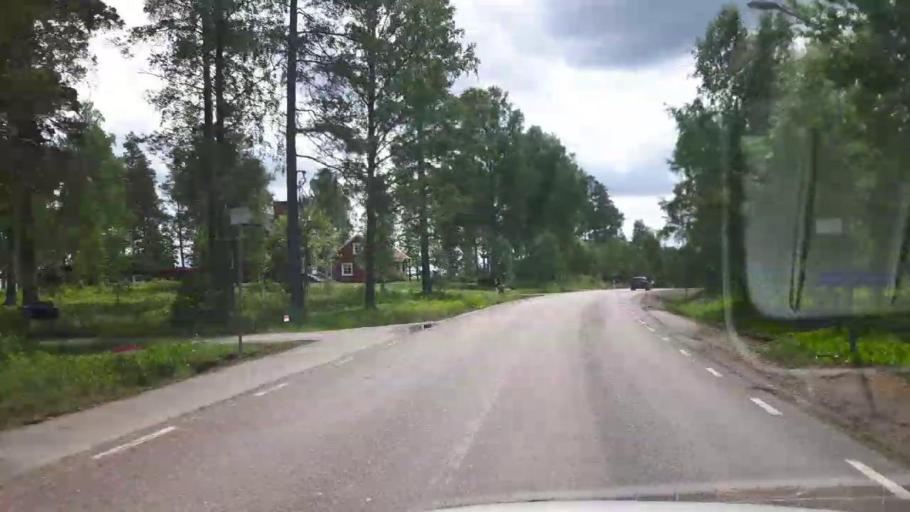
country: SE
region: Vaestmanland
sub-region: Skinnskattebergs Kommun
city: Skinnskatteberg
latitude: 59.8599
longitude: 15.8426
